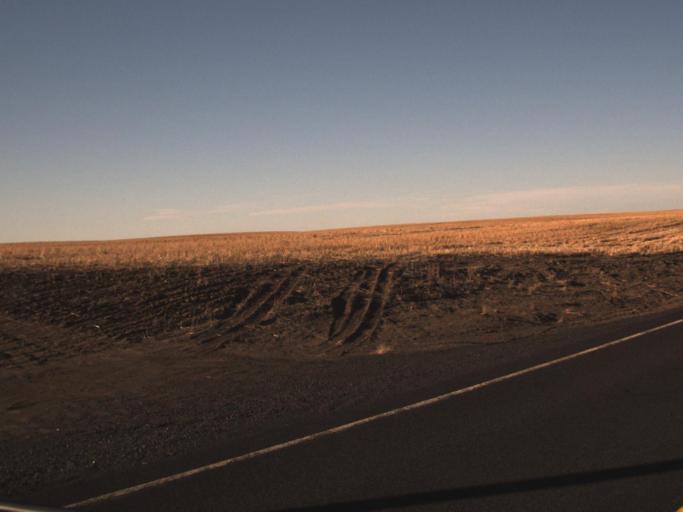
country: US
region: Washington
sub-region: Adams County
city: Ritzville
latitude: 46.8986
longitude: -118.3333
